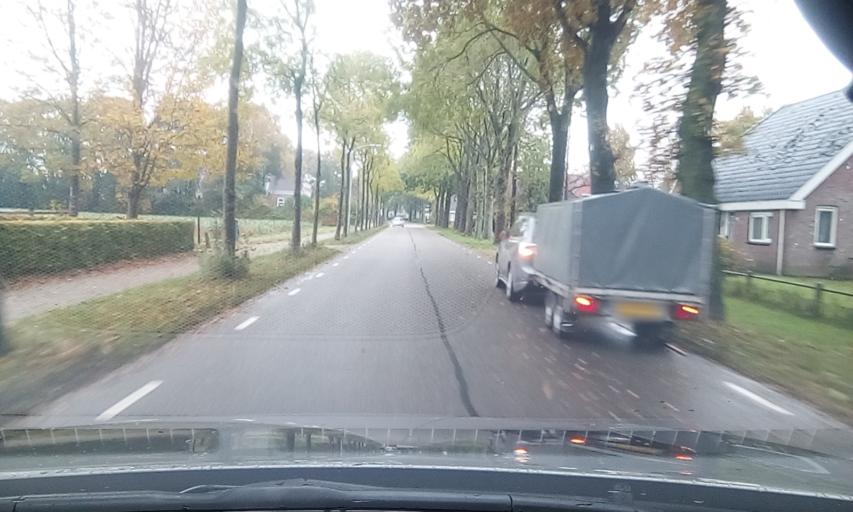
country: NL
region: Groningen
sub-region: Gemeente Haren
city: Haren
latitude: 53.2092
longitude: 6.6766
